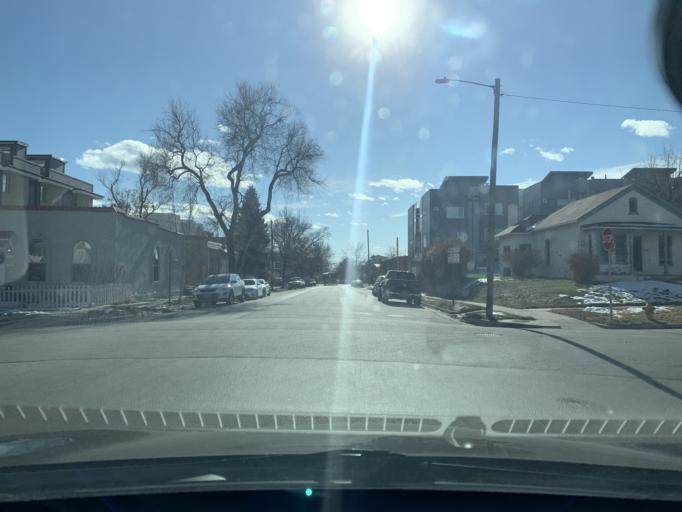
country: US
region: Colorado
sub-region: Jefferson County
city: Edgewater
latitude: 39.7526
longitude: -105.0237
